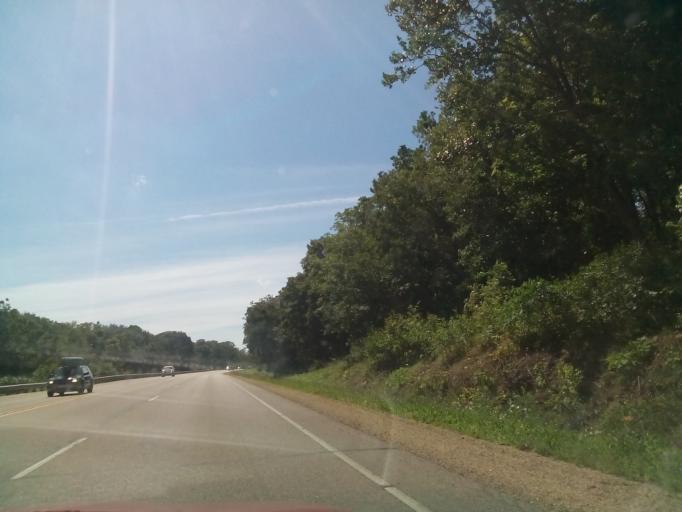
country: US
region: Wisconsin
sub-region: Green County
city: New Glarus
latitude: 42.7919
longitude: -89.6303
